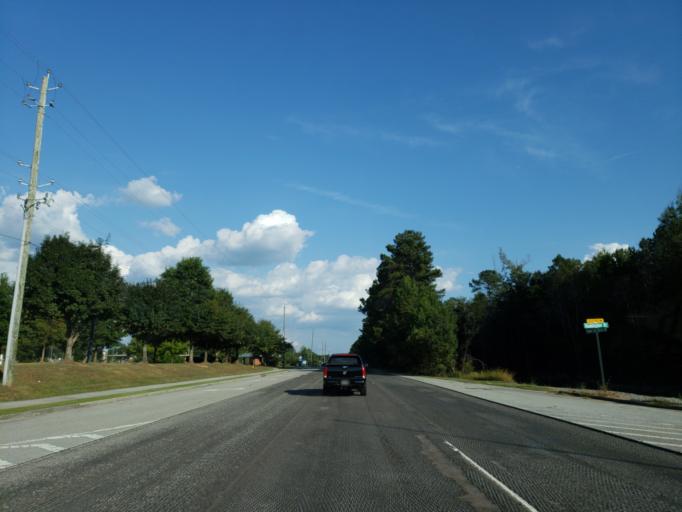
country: US
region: Georgia
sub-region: Cobb County
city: Powder Springs
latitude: 33.8675
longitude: -84.7036
